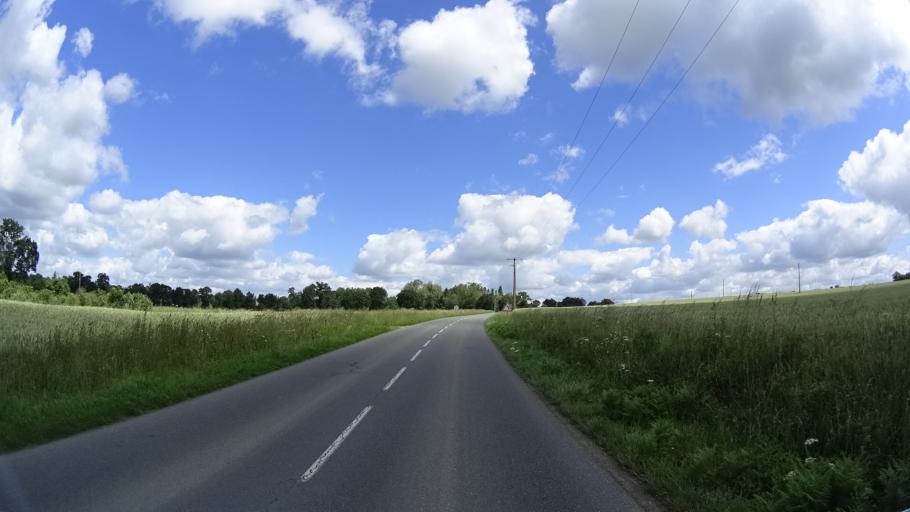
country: FR
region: Brittany
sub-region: Departement d'Ille-et-Vilaine
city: Saint-Gilles
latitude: 48.1329
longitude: -1.8261
